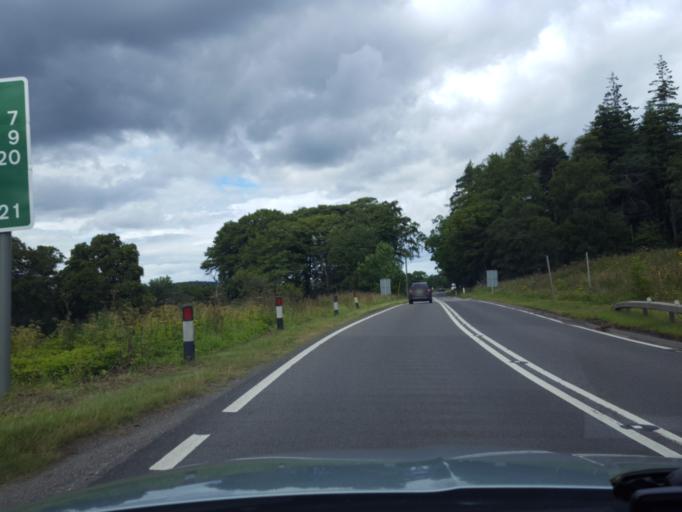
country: GB
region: Scotland
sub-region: Moray
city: Rothes
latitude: 57.4033
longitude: -3.3573
